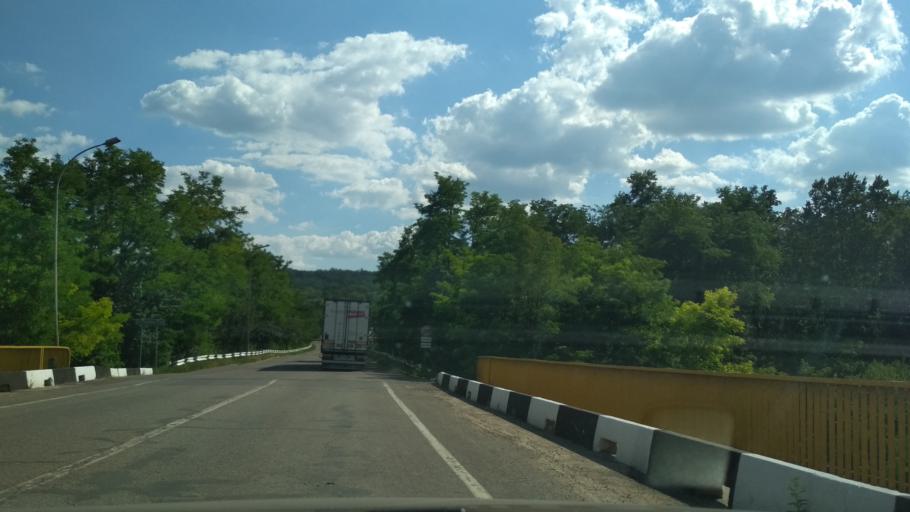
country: MD
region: Chisinau
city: Vadul lui Voda
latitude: 47.0880
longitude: 29.0906
